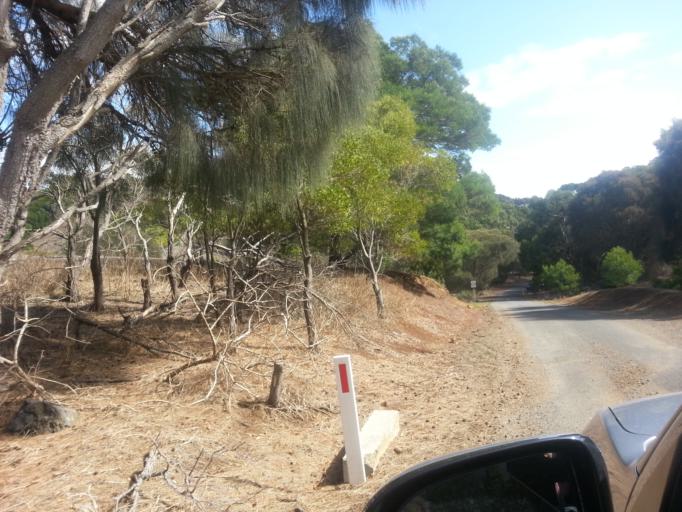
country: AU
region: Victoria
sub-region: Warrnambool
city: Warrnambool
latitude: -38.3213
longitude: 142.3645
